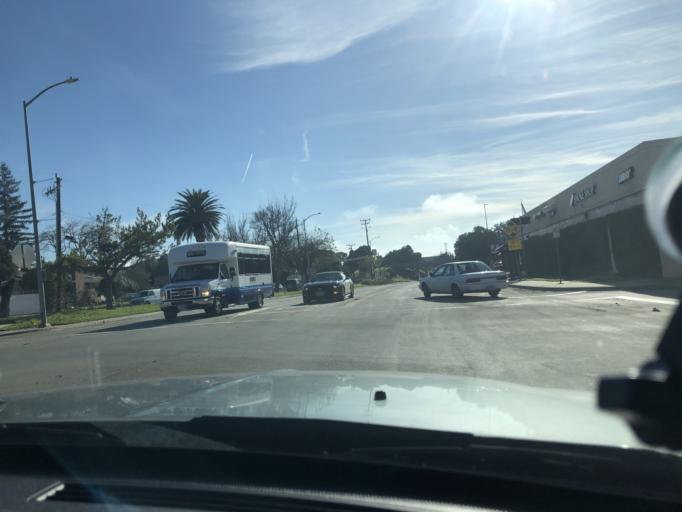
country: US
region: California
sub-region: Monterey County
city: King City
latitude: 36.2050
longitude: -121.1307
